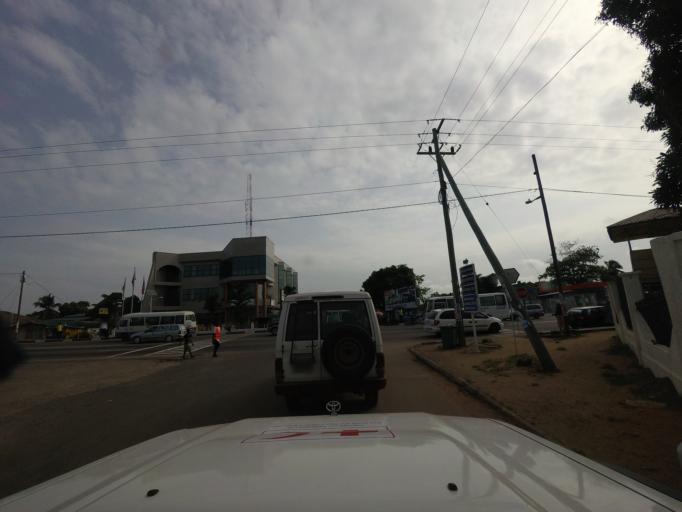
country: LR
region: Montserrado
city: Monrovia
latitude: 6.2938
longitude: -10.7851
